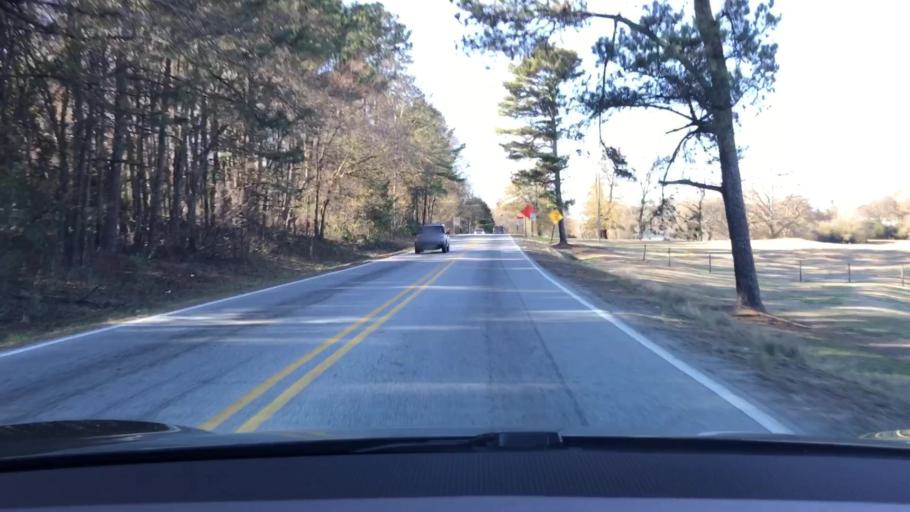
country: US
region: Georgia
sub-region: Barrow County
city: Auburn
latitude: 33.9696
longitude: -83.7808
